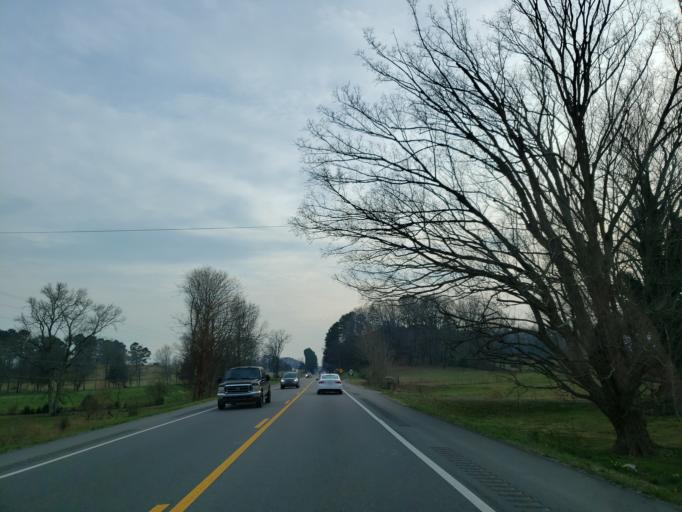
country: US
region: Tennessee
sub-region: Bradley County
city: Wildwood Lake
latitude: 35.0167
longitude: -84.9165
